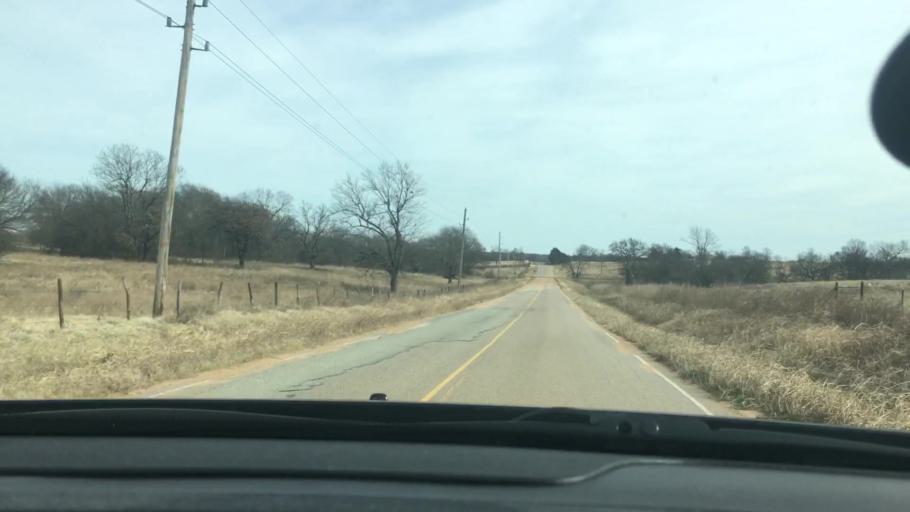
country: US
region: Oklahoma
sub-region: Murray County
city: Sulphur
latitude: 34.4050
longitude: -96.8890
